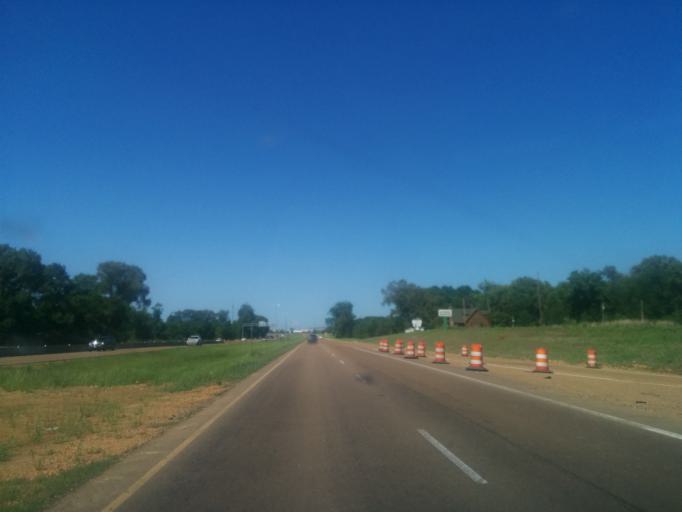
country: US
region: Mississippi
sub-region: Madison County
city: Madison
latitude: 32.5185
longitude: -90.1005
